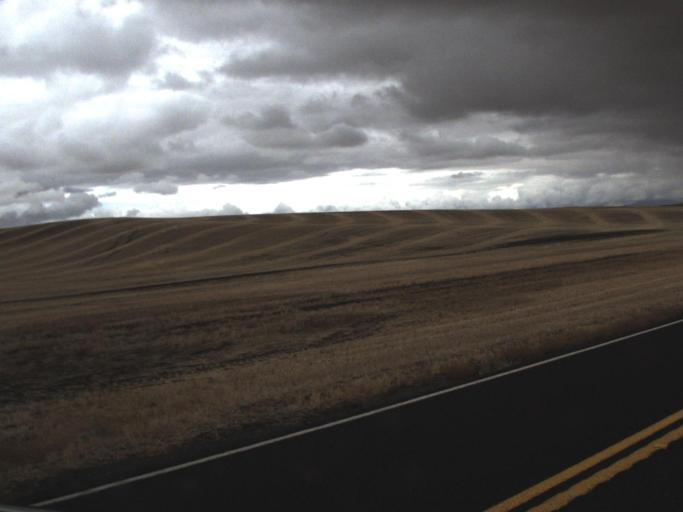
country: US
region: Washington
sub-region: Whitman County
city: Colfax
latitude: 47.1635
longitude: -117.2739
